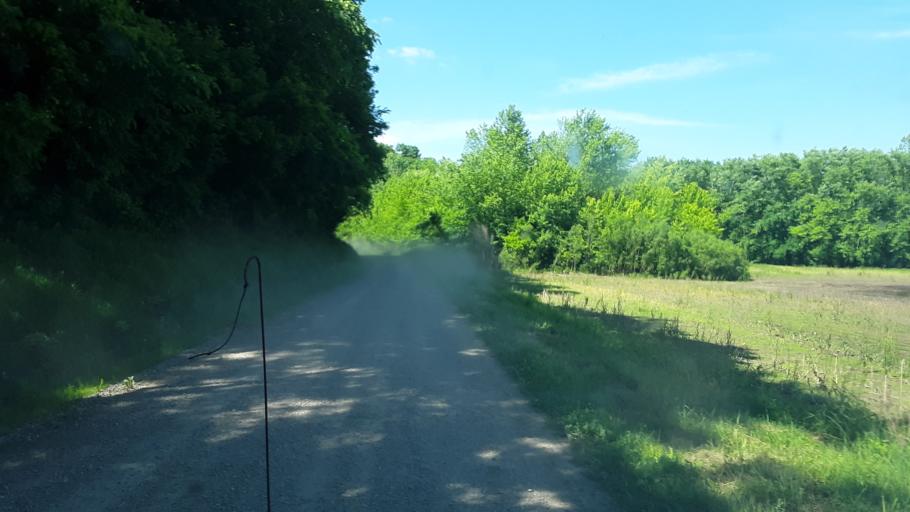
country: US
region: Ohio
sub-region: Coshocton County
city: West Lafayette
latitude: 40.1960
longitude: -81.6896
